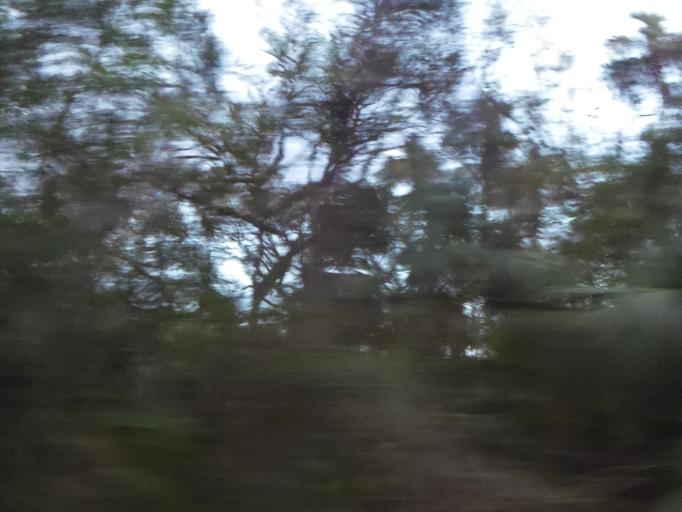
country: US
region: Florida
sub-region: Duval County
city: Atlantic Beach
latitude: 30.3719
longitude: -81.4012
